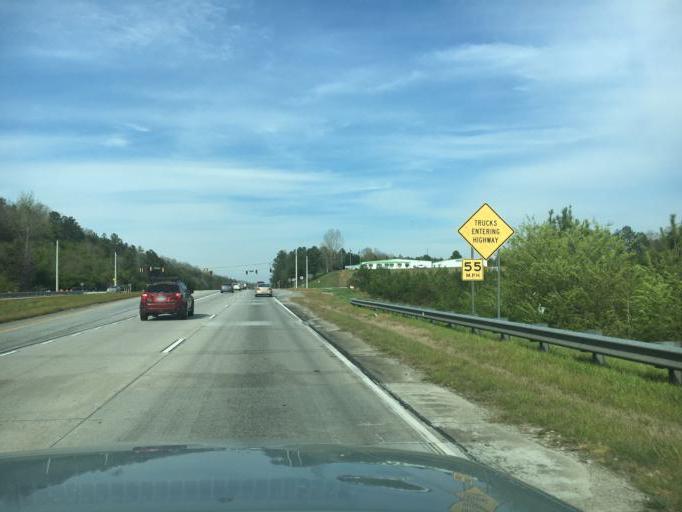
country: US
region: Georgia
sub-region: Hall County
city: Gainesville
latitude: 34.3402
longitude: -83.7740
